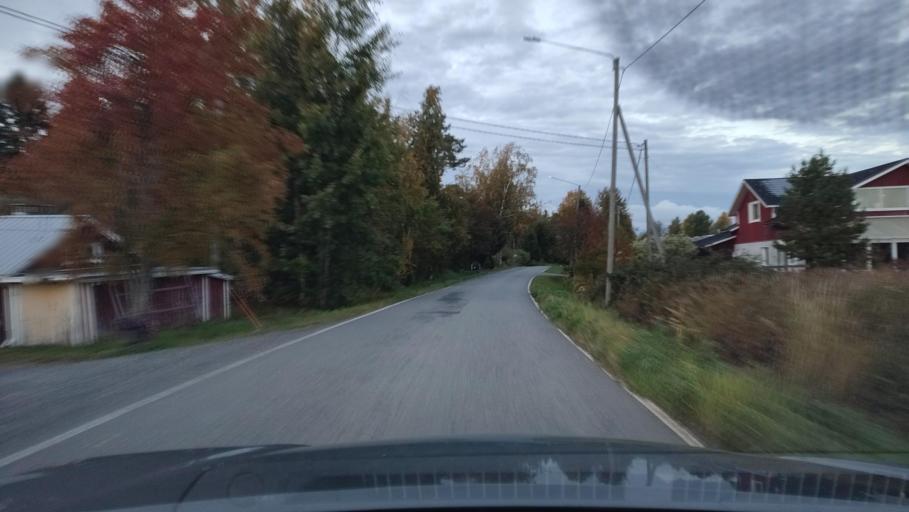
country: FI
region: Ostrobothnia
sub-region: Sydosterbotten
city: Kristinestad
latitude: 62.2714
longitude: 21.5101
